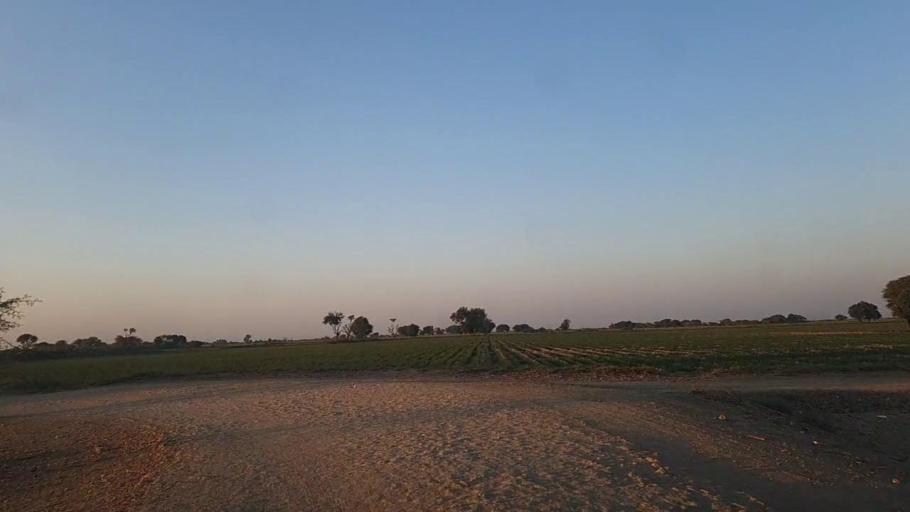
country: PK
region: Sindh
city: Naukot
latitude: 25.0562
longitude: 69.4071
